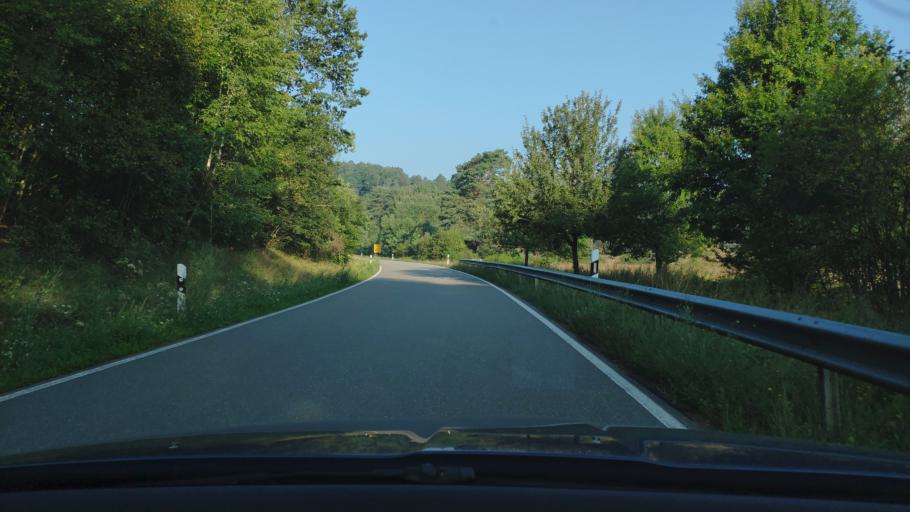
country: DE
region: Rheinland-Pfalz
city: Fischbach
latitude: 49.0698
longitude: 7.7119
